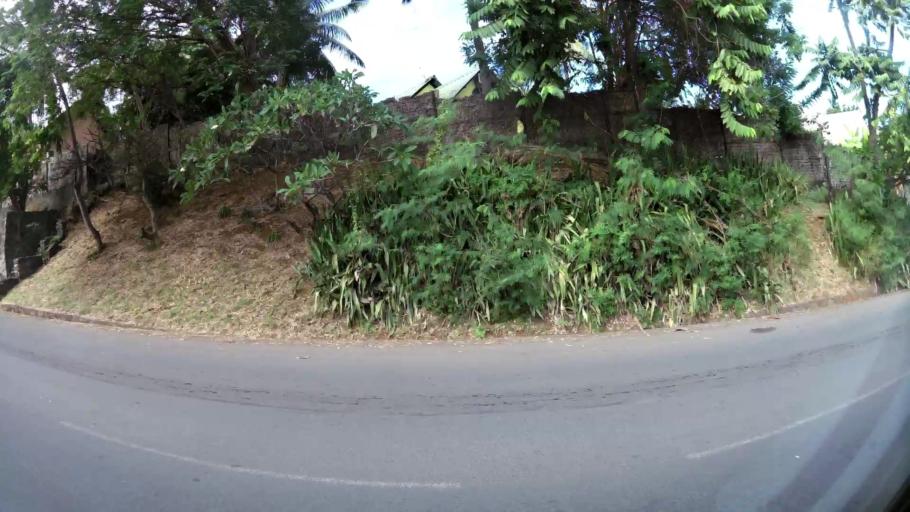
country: YT
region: Mamoudzou
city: Mamoudzou
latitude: -12.7836
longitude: 45.2234
